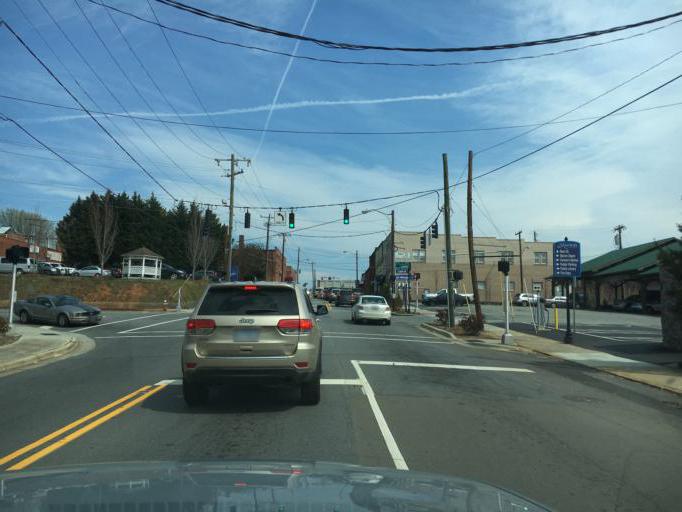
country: US
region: North Carolina
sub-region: McDowell County
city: Marion
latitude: 35.6823
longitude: -82.0100
